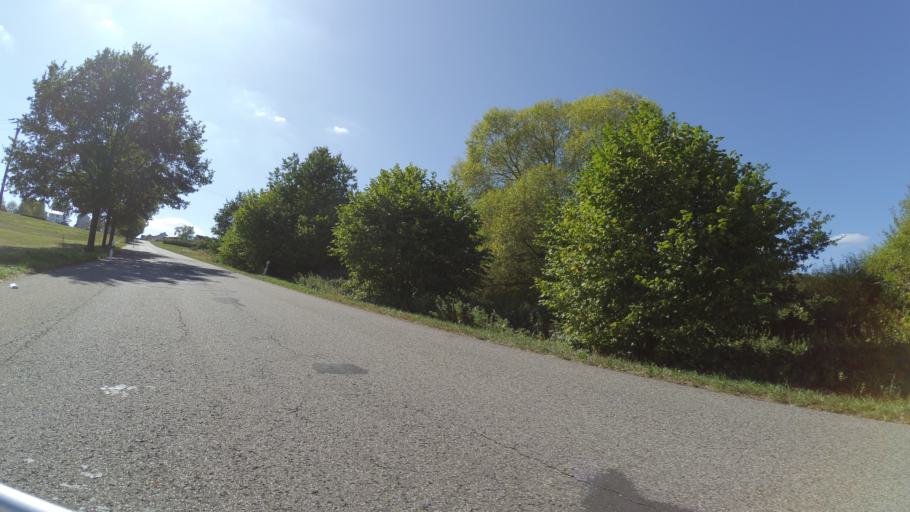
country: DE
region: Saarland
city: Lebach
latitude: 49.3821
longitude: 6.8975
